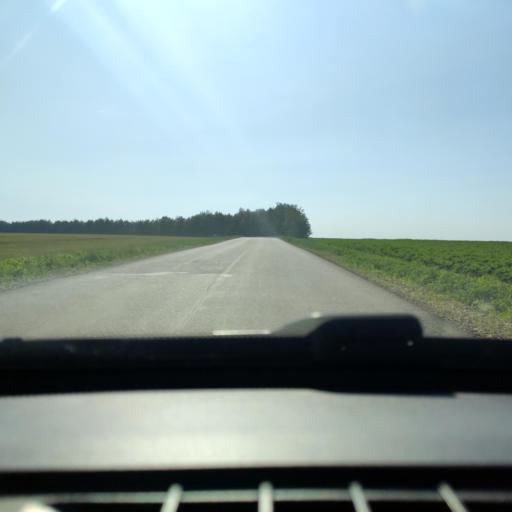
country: RU
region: Voronezj
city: Pereleshinskiy
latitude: 51.6449
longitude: 40.2974
